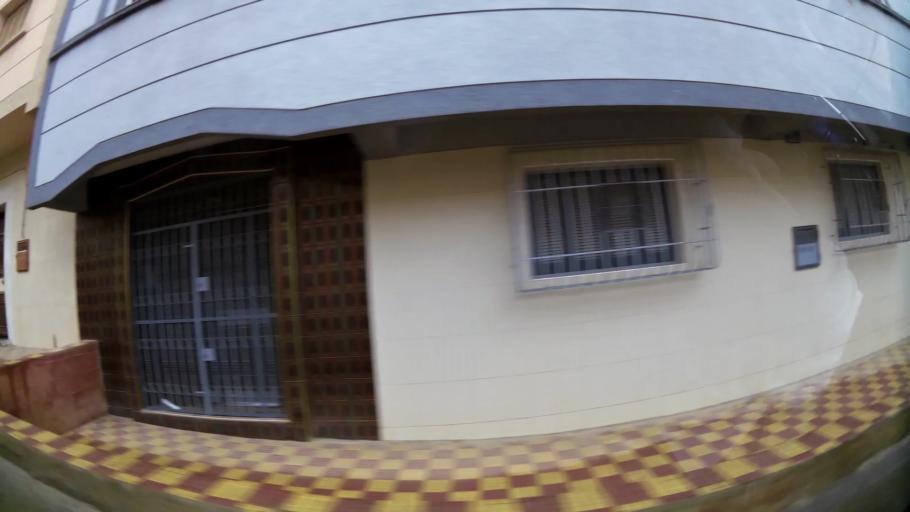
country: MA
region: Oriental
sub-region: Nador
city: Nador
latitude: 35.1796
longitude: -2.9381
